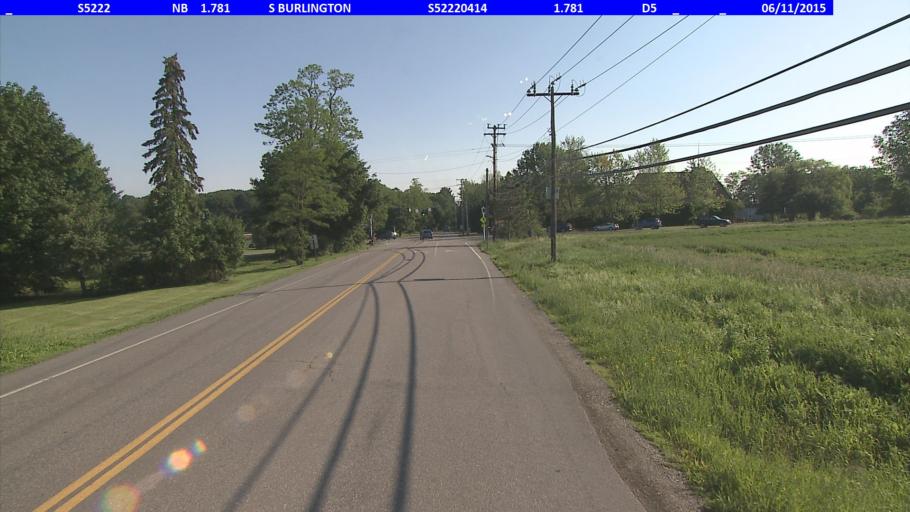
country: US
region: Vermont
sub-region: Chittenden County
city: South Burlington
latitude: 44.4422
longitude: -73.1892
